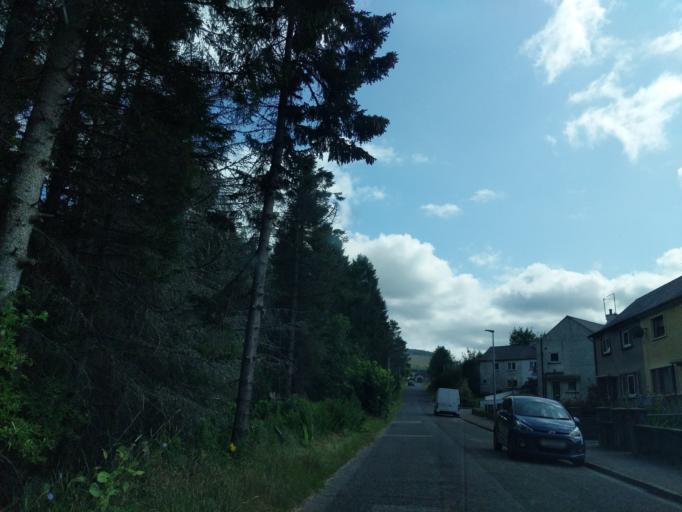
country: GB
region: Scotland
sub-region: Moray
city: Rothes
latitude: 57.4894
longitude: -3.1830
